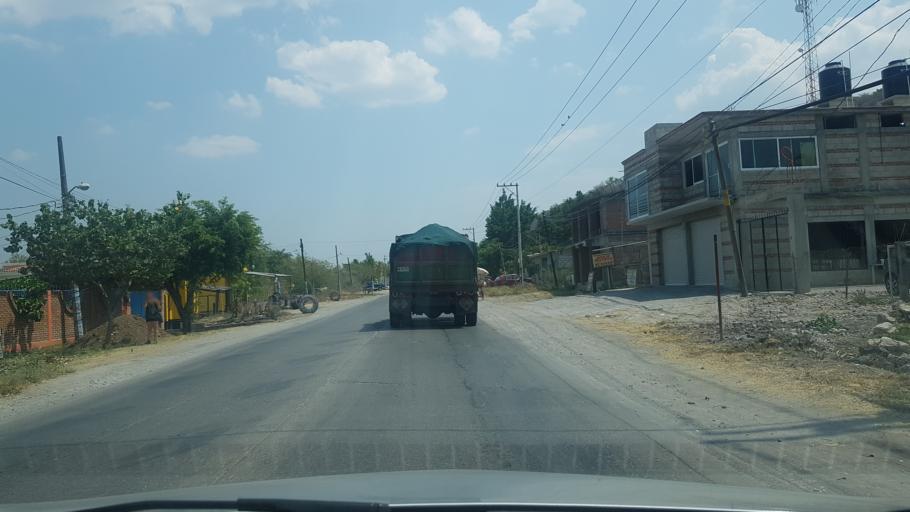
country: MX
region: Morelos
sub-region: Tlaltizapan de Zapata
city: Colonia Palo Prieto (Chipitongo)
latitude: 18.7142
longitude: -99.1185
